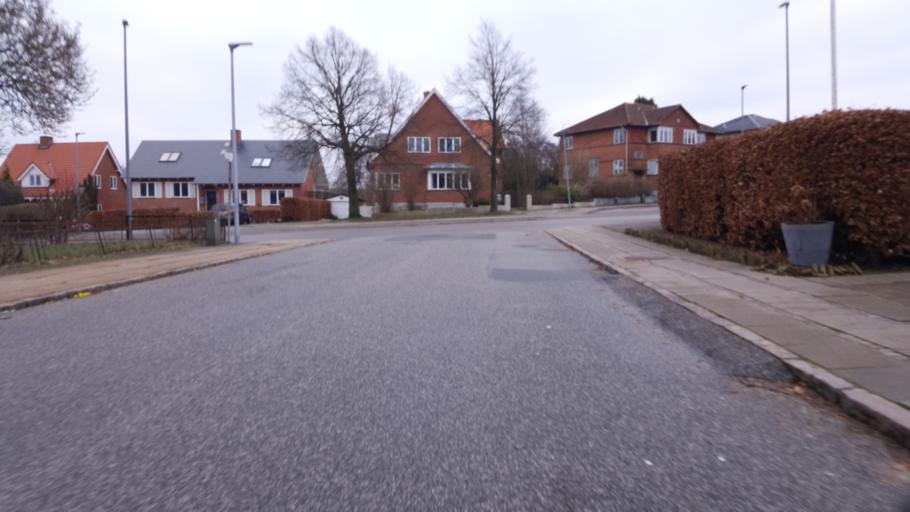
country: DK
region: South Denmark
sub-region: Kolding Kommune
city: Kolding
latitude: 55.4822
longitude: 9.4790
